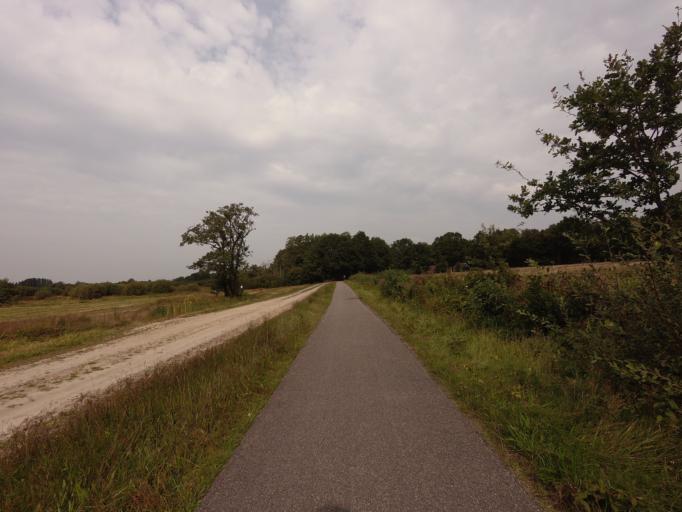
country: NL
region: Drenthe
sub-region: Gemeente Tynaarlo
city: Tynaarlo
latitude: 53.0194
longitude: 6.6329
